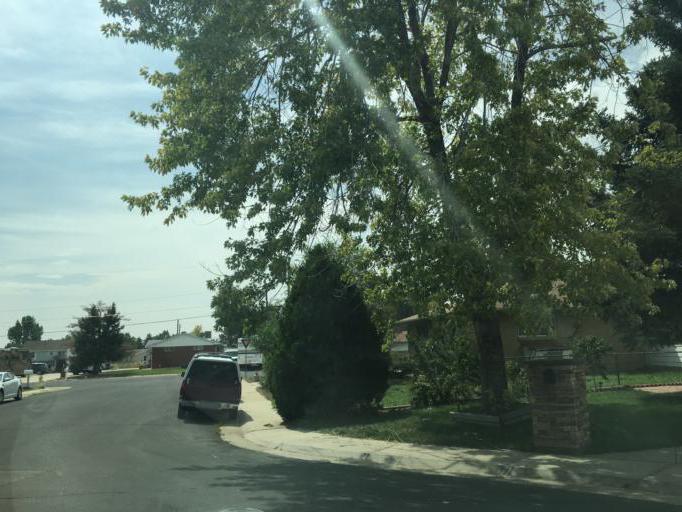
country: US
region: Colorado
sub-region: Adams County
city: Aurora
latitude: 39.7326
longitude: -104.8048
